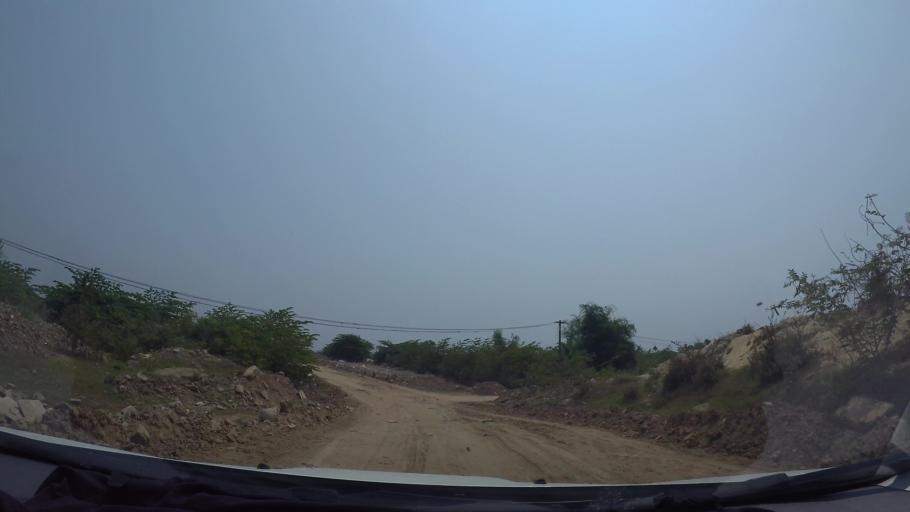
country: VN
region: Da Nang
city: Cam Le
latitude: 15.9966
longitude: 108.2240
